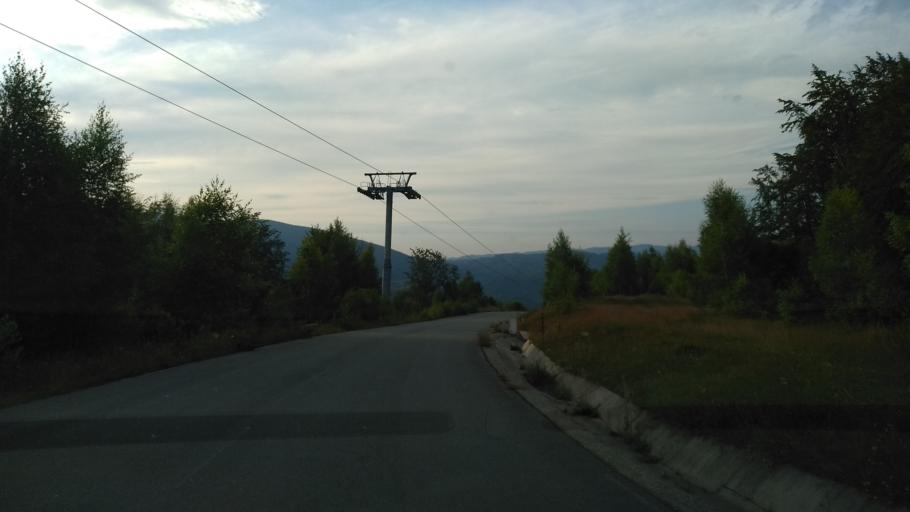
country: RO
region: Hunedoara
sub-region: Municipiul  Vulcan
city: Jiu-Paroseni
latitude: 45.3488
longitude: 23.2903
